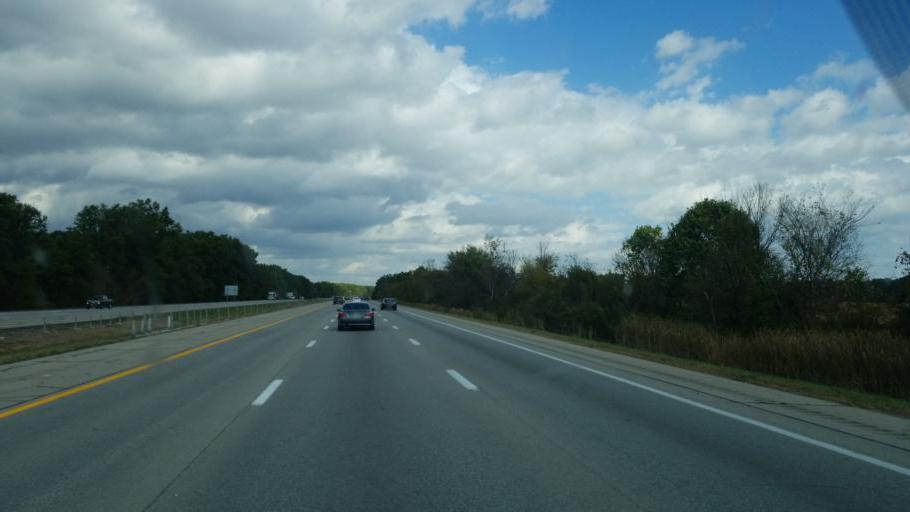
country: US
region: Ohio
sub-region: Delaware County
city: Sunbury
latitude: 40.2867
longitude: -82.9253
